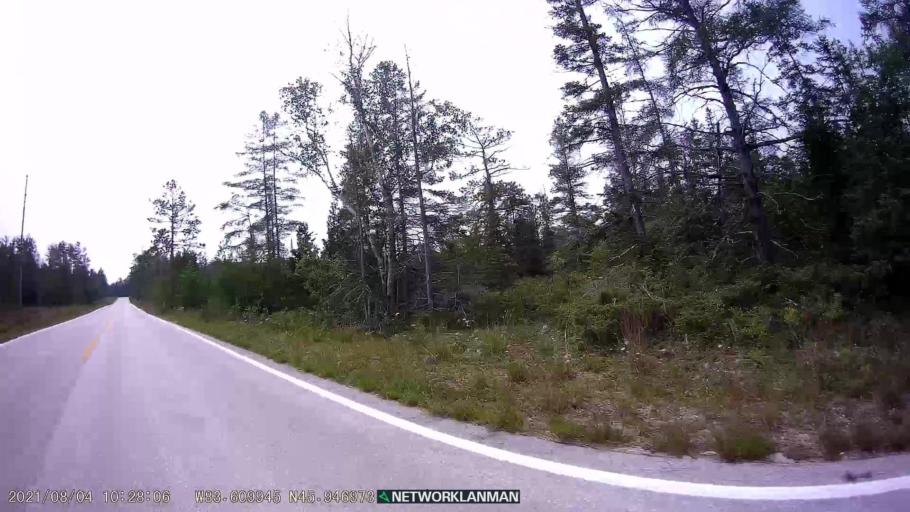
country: CA
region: Ontario
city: Thessalon
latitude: 45.9468
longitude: -83.6100
